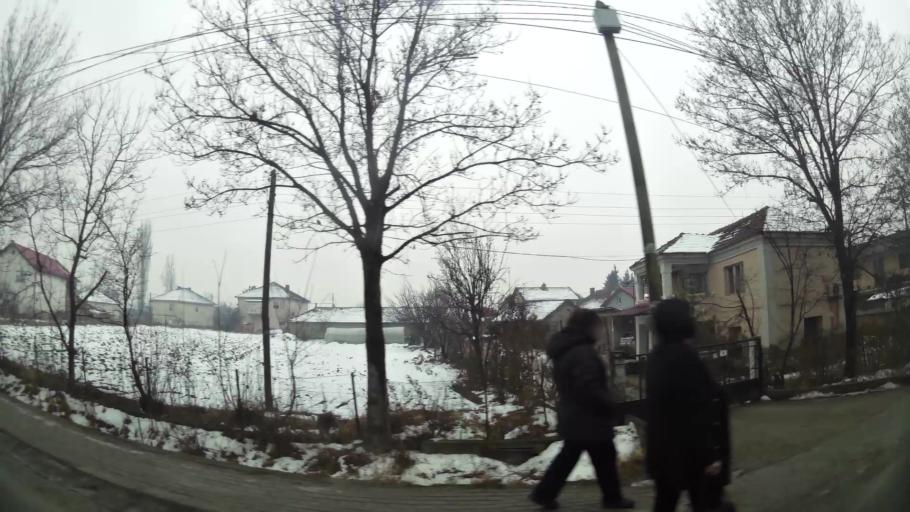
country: MK
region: Petrovec
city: Petrovec
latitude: 41.9399
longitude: 21.6133
